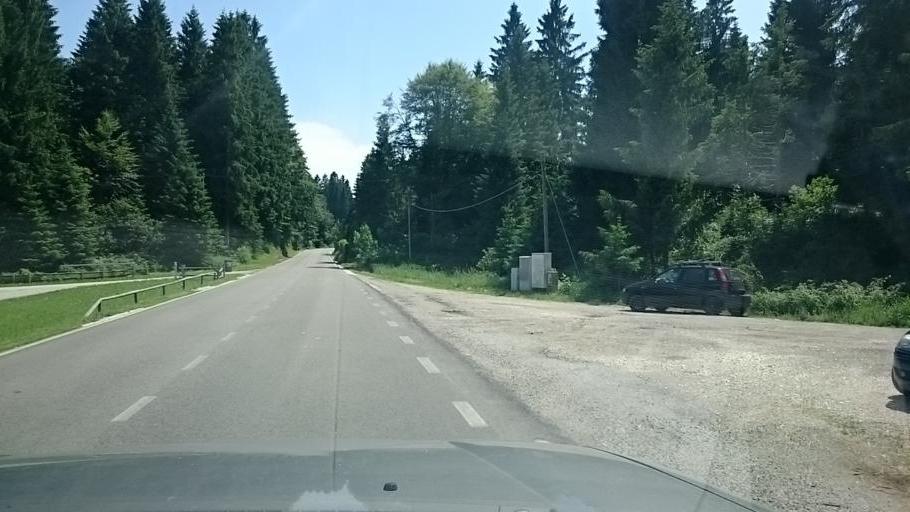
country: IT
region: Veneto
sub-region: Provincia di Vicenza
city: Gallio
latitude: 45.8534
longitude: 11.5480
